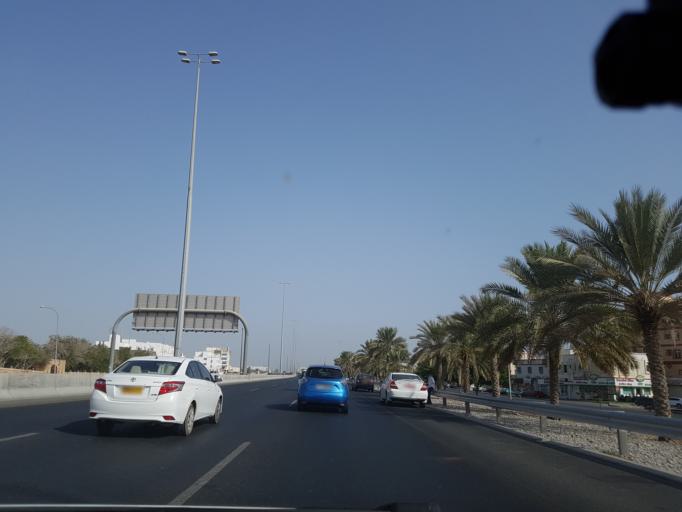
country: OM
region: Muhafazat Masqat
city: As Sib al Jadidah
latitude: 23.6240
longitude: 58.2380
